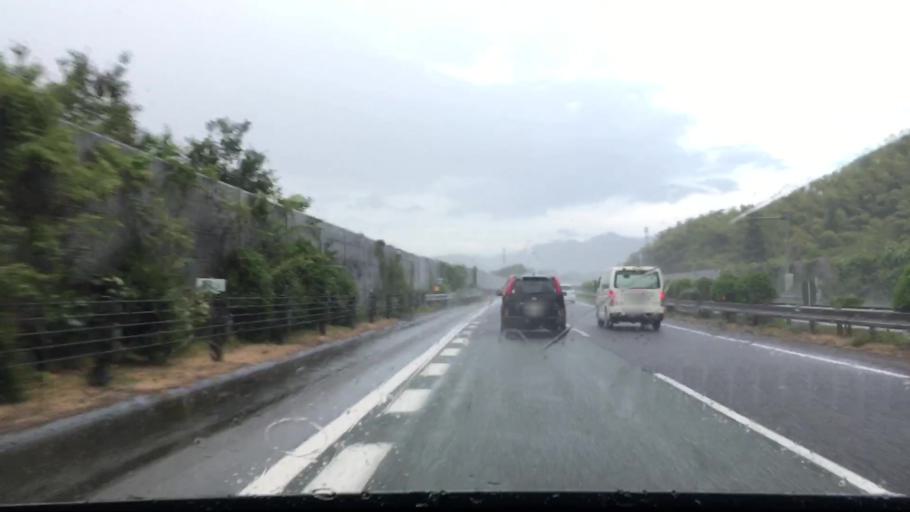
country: JP
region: Fukuoka
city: Kitakyushu
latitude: 33.8088
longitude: 130.8261
